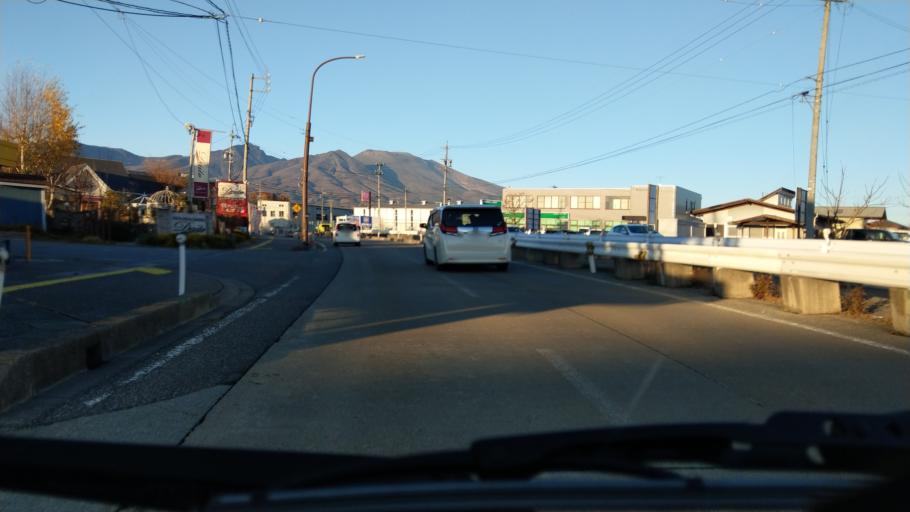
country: JP
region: Nagano
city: Komoro
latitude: 36.2855
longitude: 138.4742
